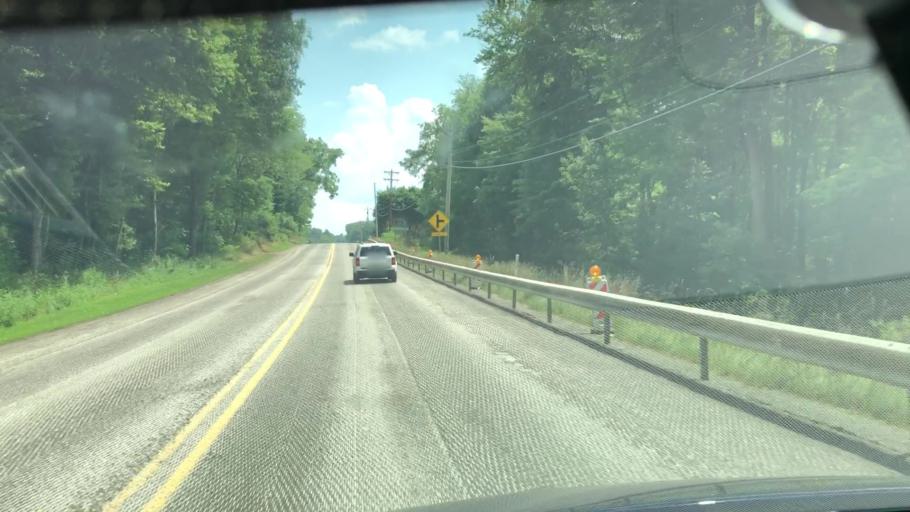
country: US
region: Pennsylvania
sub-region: Butler County
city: Saxonburg
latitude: 40.7961
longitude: -79.8186
